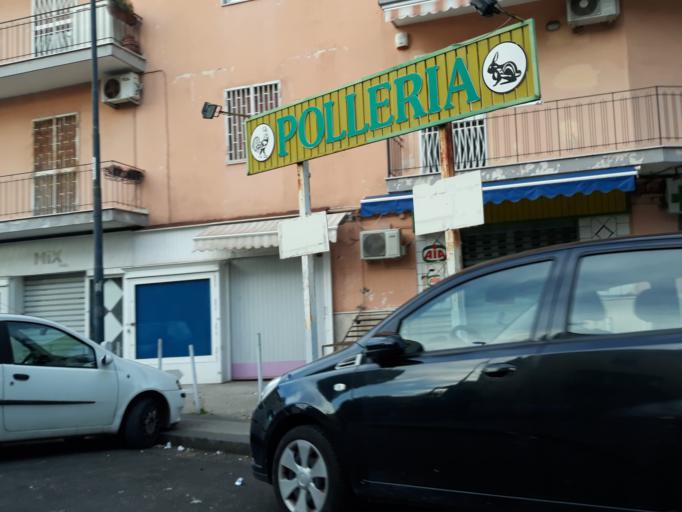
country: IT
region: Campania
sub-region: Provincia di Napoli
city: Mugnano di Napoli
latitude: 40.8906
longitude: 14.2314
